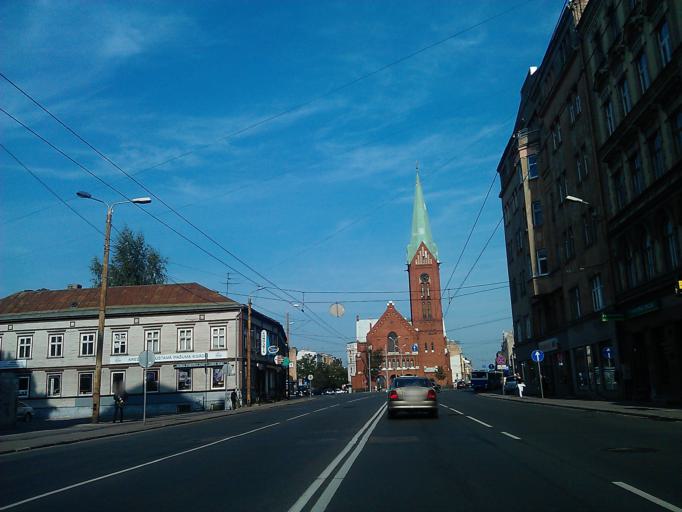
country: LV
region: Riga
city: Riga
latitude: 56.9617
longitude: 24.1339
